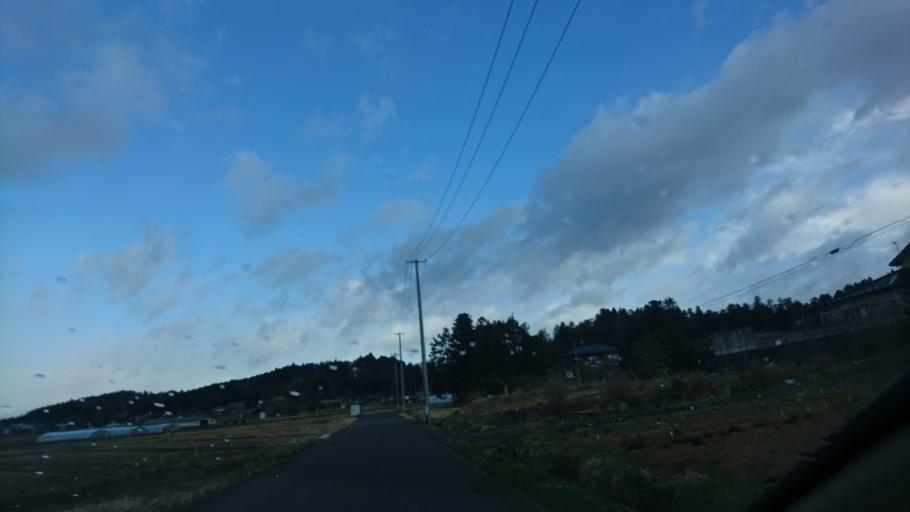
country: JP
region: Iwate
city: Ichinoseki
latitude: 38.7911
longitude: 141.0311
